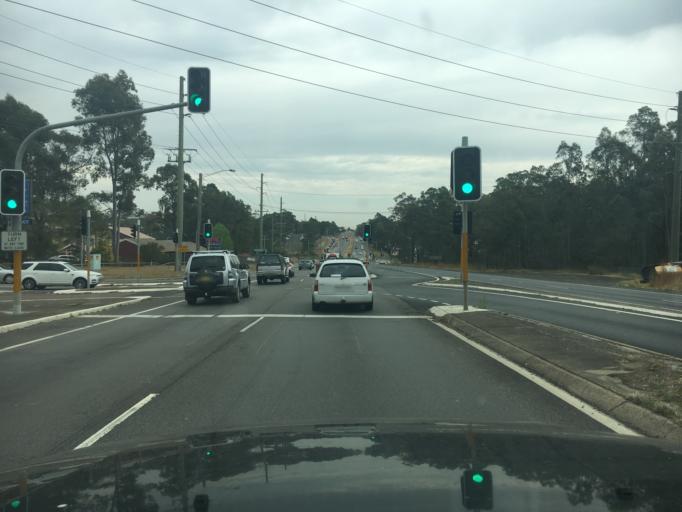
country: AU
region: New South Wales
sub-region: Maitland Municipality
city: East Maitland
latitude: -32.7642
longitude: 151.5980
